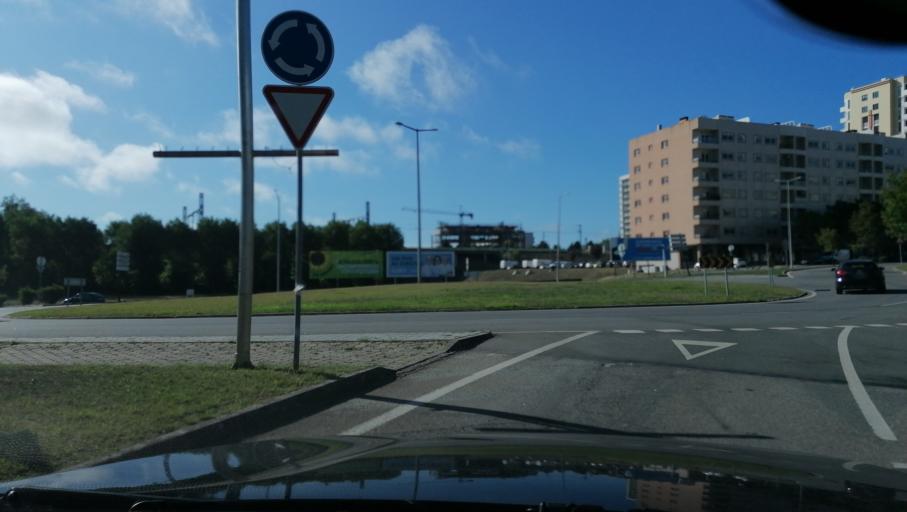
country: PT
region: Aveiro
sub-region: Aveiro
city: Aveiro
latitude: 40.6384
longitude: -8.6406
